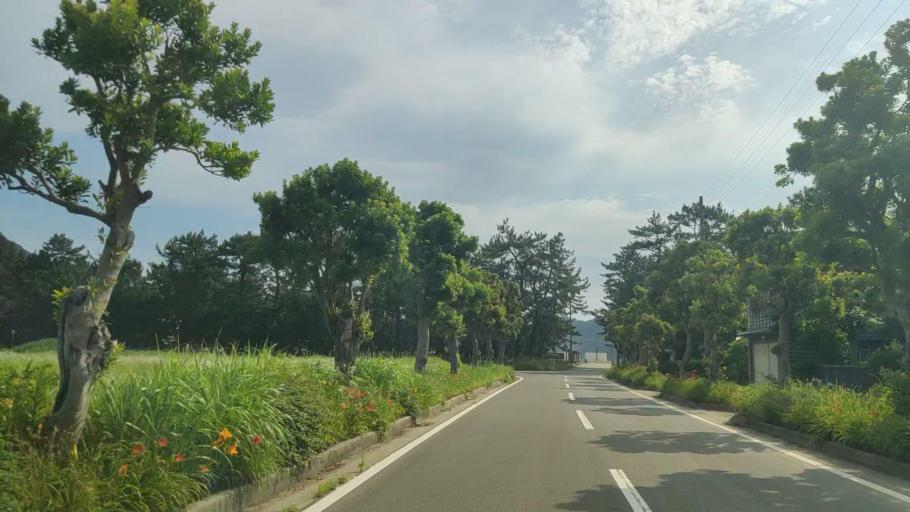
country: JP
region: Hyogo
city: Toyooka
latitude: 35.6437
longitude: 134.8347
